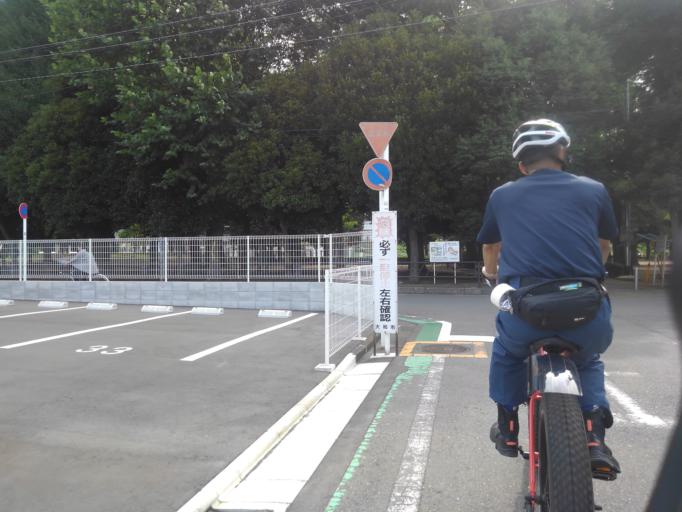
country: JP
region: Kanagawa
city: Minami-rinkan
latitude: 35.4672
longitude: 139.4615
